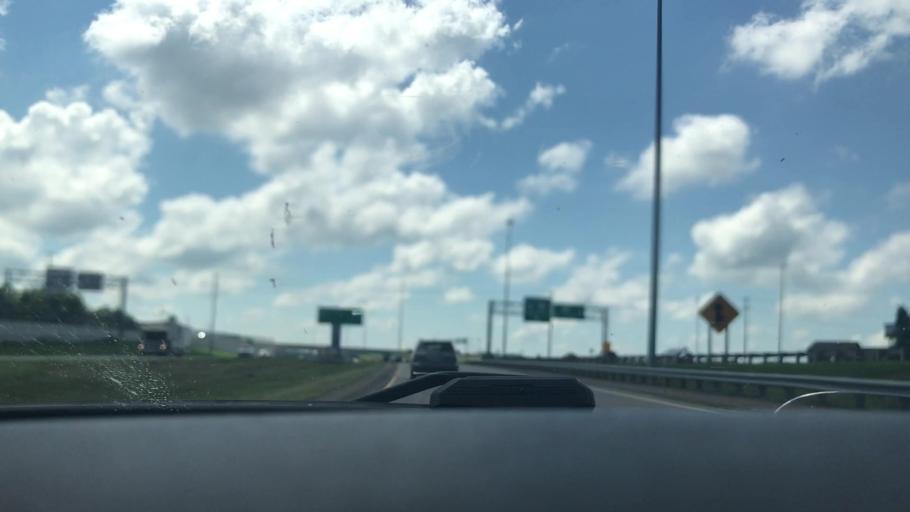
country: US
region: Wisconsin
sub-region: Eau Claire County
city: Altoona
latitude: 44.7934
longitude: -91.4557
